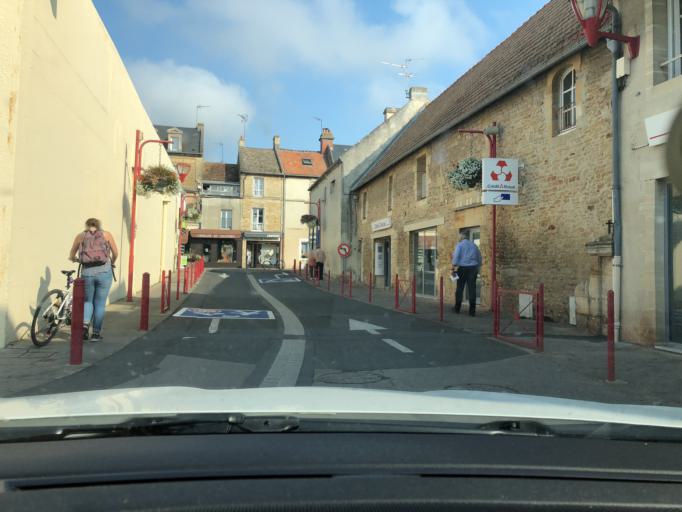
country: FR
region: Lower Normandy
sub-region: Departement du Calvados
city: Douvres-la-Delivrande
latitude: 49.2974
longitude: -0.3739
